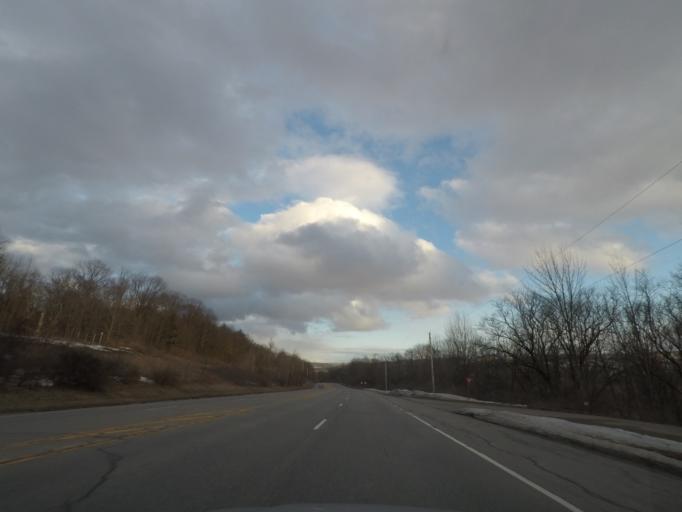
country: US
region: New York
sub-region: Montgomery County
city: Saint Johnsville
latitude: 43.0117
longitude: -74.7677
